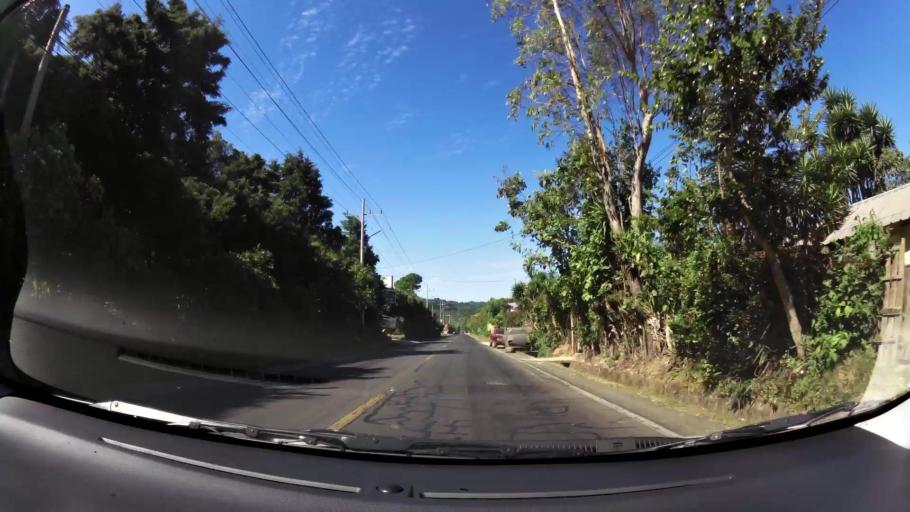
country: SV
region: Ahuachapan
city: Concepcion de Ataco
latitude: 13.8484
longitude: -89.8273
